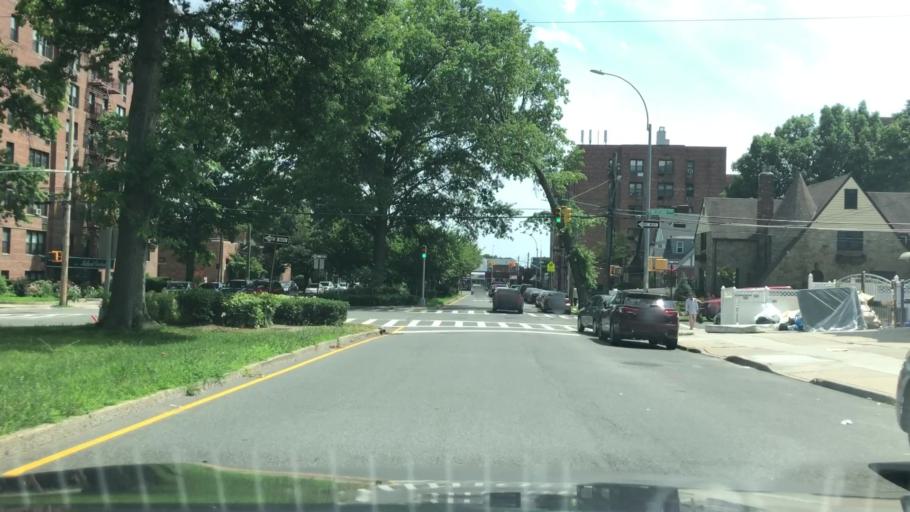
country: US
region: New York
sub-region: Queens County
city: Jamaica
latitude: 40.7143
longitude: -73.7830
